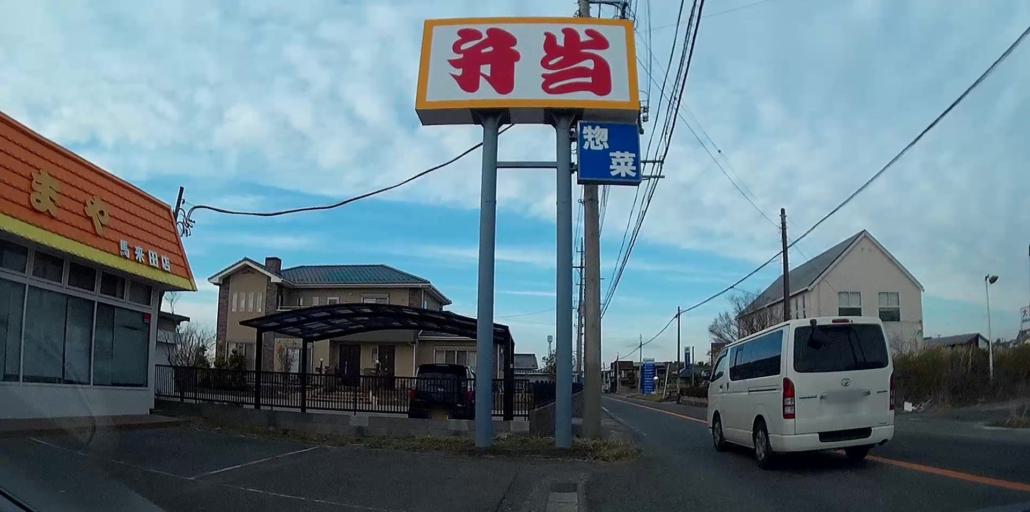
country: JP
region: Chiba
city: Kisarazu
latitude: 35.3611
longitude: 140.0577
